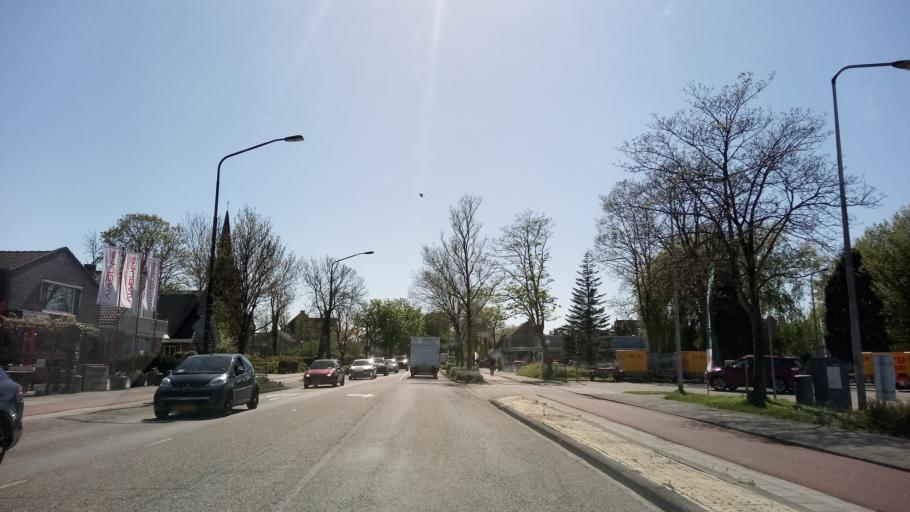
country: NL
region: North Holland
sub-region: Gemeente Heerhugowaard
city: Heerhugowaard
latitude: 52.6681
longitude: 4.8424
